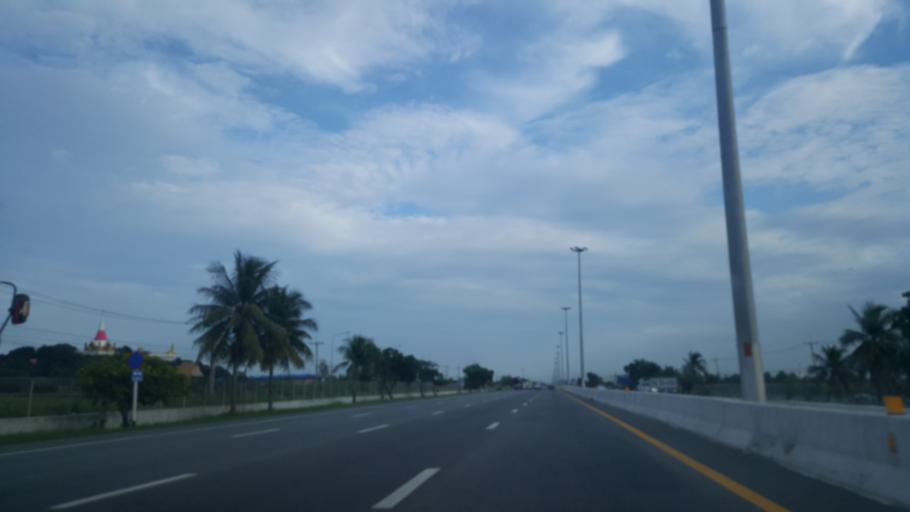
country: TH
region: Chachoengsao
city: Bang Pakong
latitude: 13.5334
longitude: 101.0140
